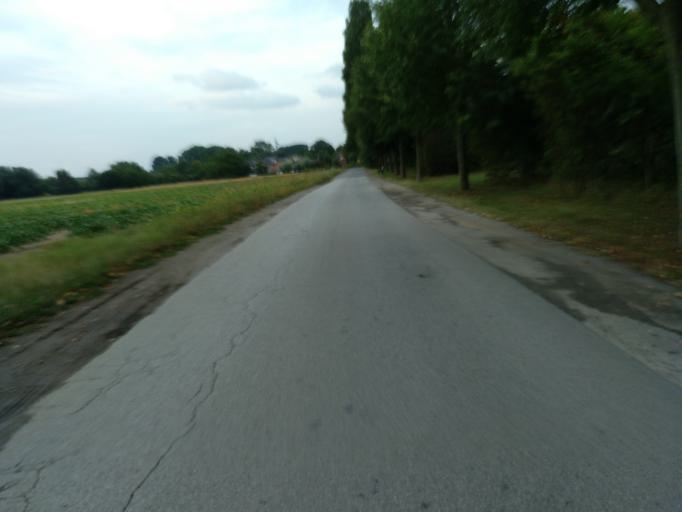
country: DE
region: North Rhine-Westphalia
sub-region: Regierungsbezirk Dusseldorf
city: Krefeld
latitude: 51.4081
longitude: 6.5469
